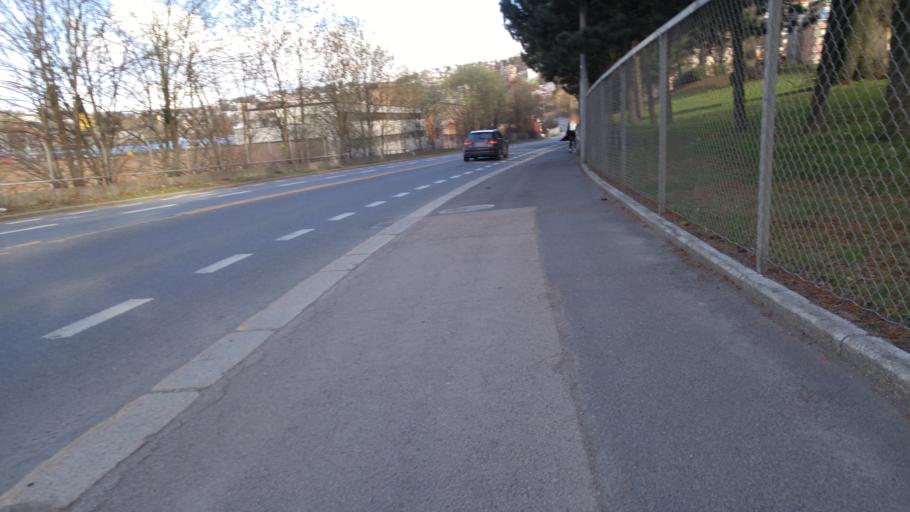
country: NO
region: Oslo
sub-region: Oslo
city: Oslo
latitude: 59.9047
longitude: 10.7713
